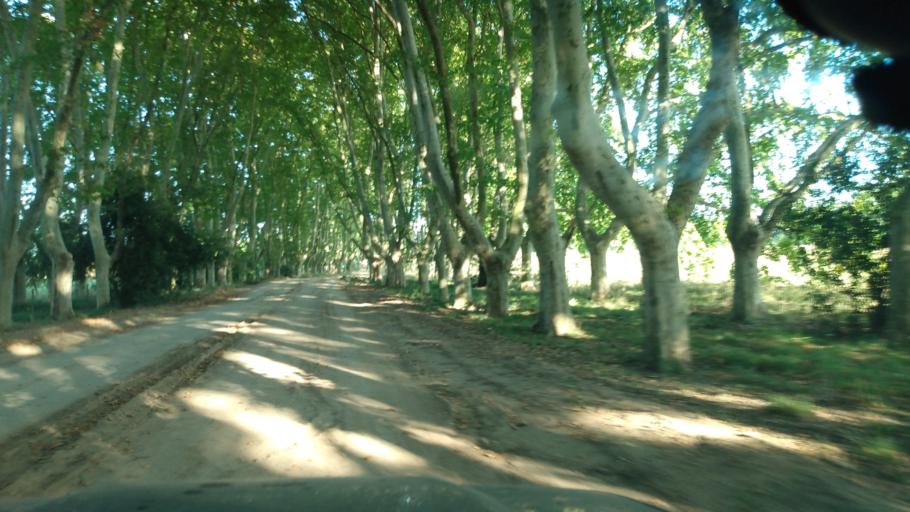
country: AR
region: Buenos Aires
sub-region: Partido de Lujan
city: Lujan
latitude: -34.5811
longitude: -59.0836
